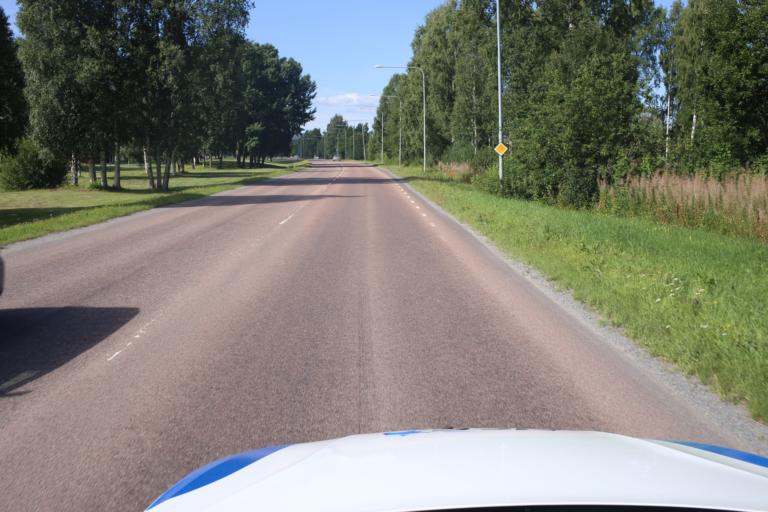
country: SE
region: Vaesterbotten
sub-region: Skelleftea Kommun
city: Skelleftea
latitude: 64.7451
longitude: 20.9727
